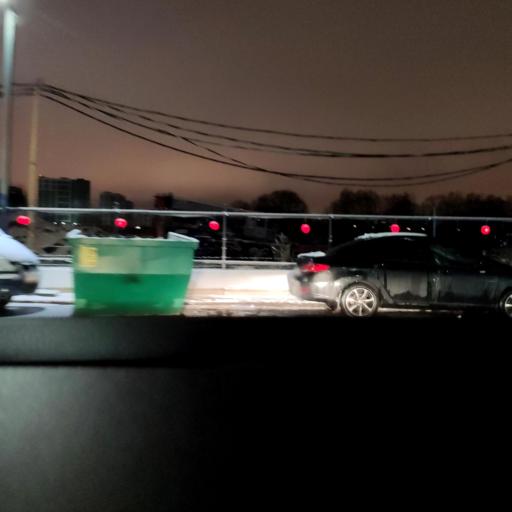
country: RU
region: Moskovskaya
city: Pavshino
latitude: 55.8633
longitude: 37.3736
